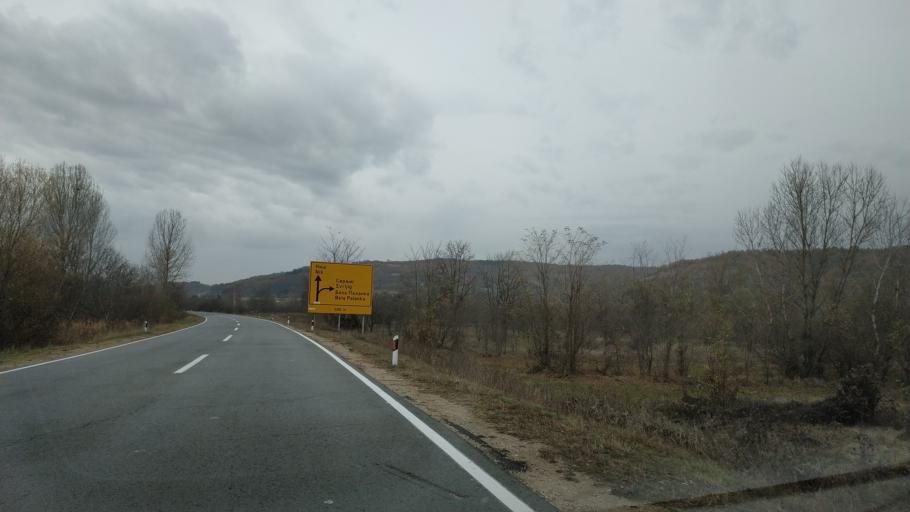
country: RS
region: Central Serbia
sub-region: Pirotski Okrug
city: Bela Palanka
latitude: 43.2298
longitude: 22.3250
